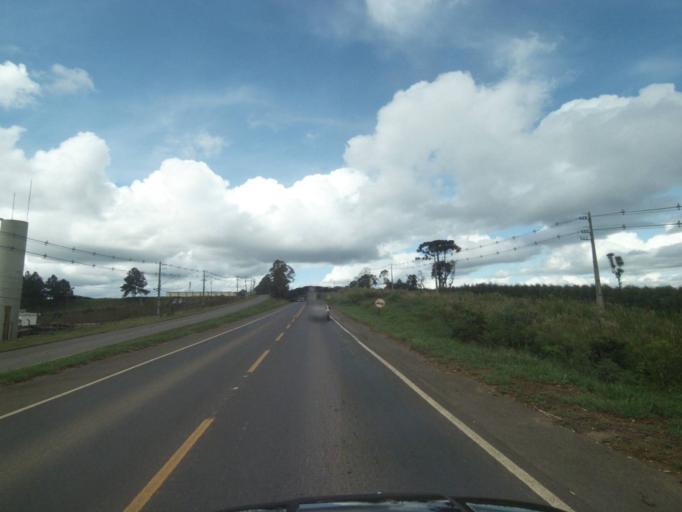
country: BR
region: Parana
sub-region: Telemaco Borba
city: Telemaco Borba
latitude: -24.3710
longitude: -50.6616
